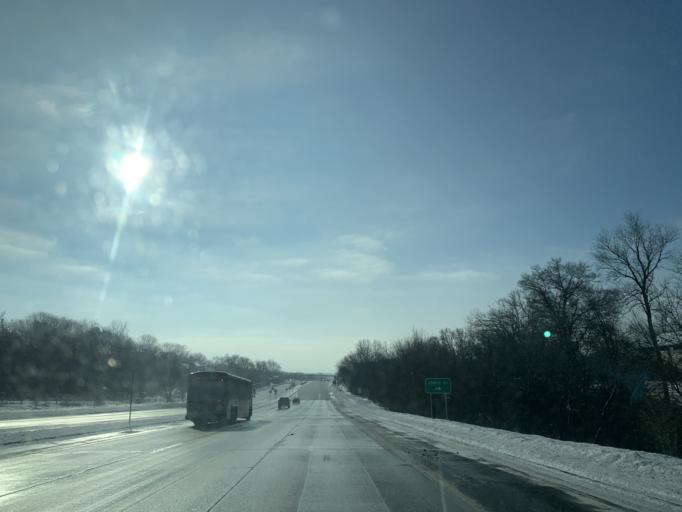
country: US
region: Minnesota
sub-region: Dakota County
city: Apple Valley
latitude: 44.7525
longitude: -93.2180
